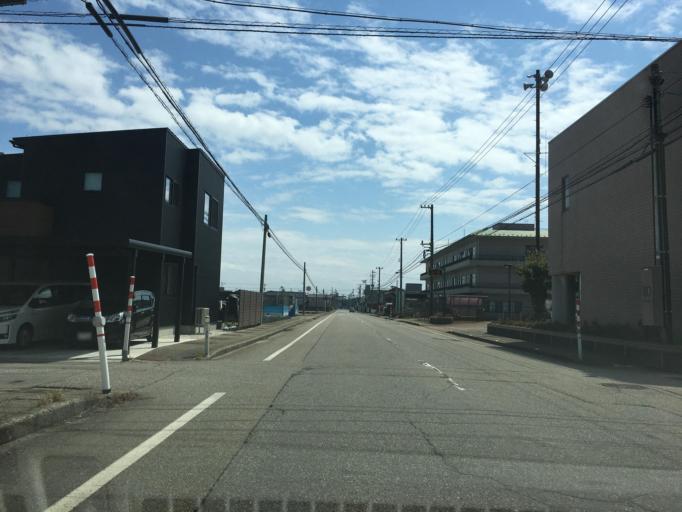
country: JP
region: Toyama
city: Nishishinminato
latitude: 36.8013
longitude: 137.0535
